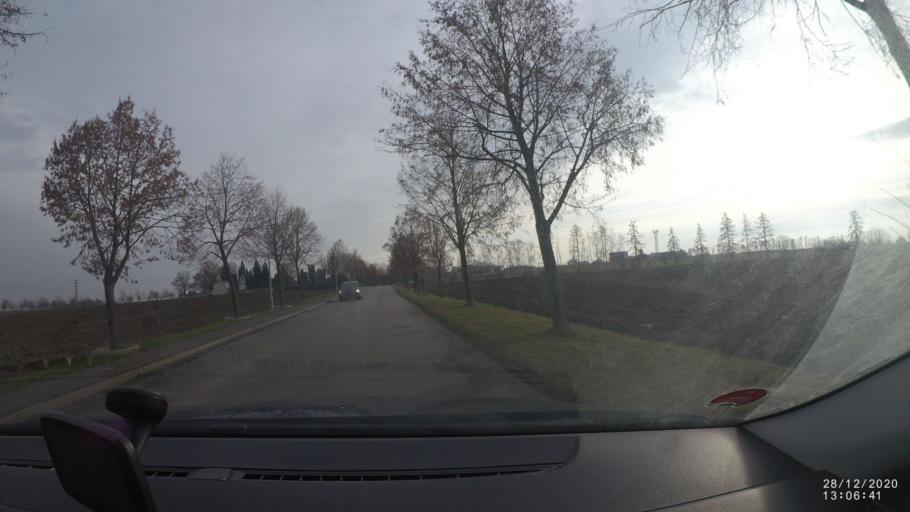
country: CZ
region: Central Bohemia
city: Zelenec
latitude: 50.1415
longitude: 14.6558
